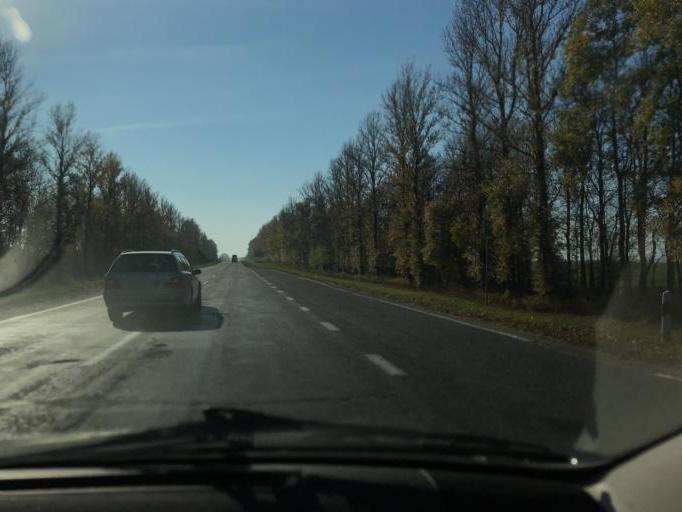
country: BY
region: Minsk
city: Salihorsk
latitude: 52.9006
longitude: 27.4757
